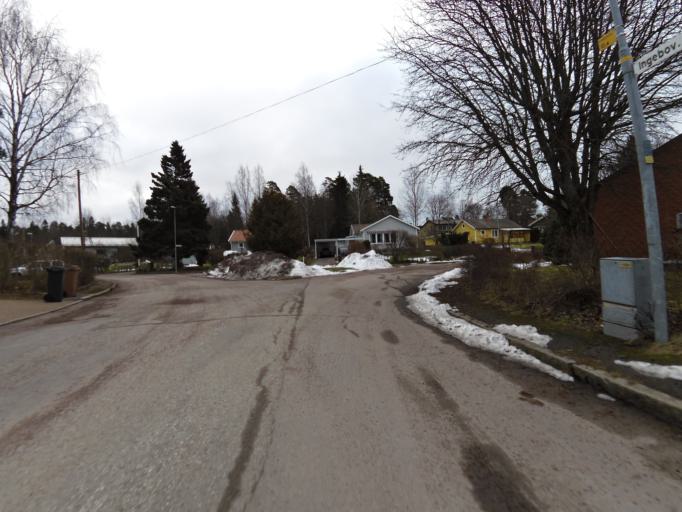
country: SE
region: Gaevleborg
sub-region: Gavle Kommun
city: Gavle
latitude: 60.6618
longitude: 17.1214
